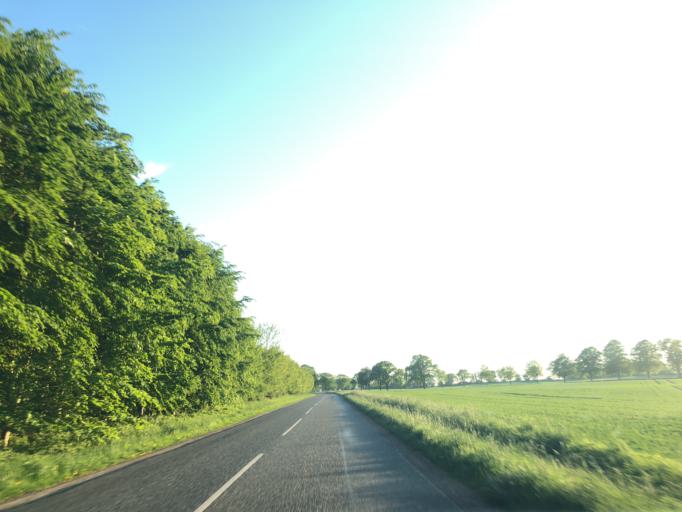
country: DK
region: Zealand
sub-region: Koge Kommune
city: Borup
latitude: 55.4227
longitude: 11.9368
